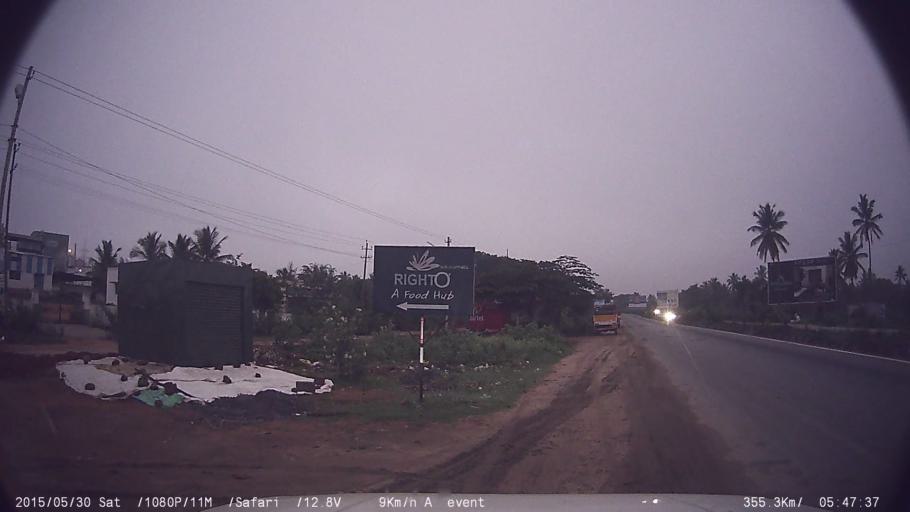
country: IN
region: Karnataka
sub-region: Mandya
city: Mandya
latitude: 12.4960
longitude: 76.8033
